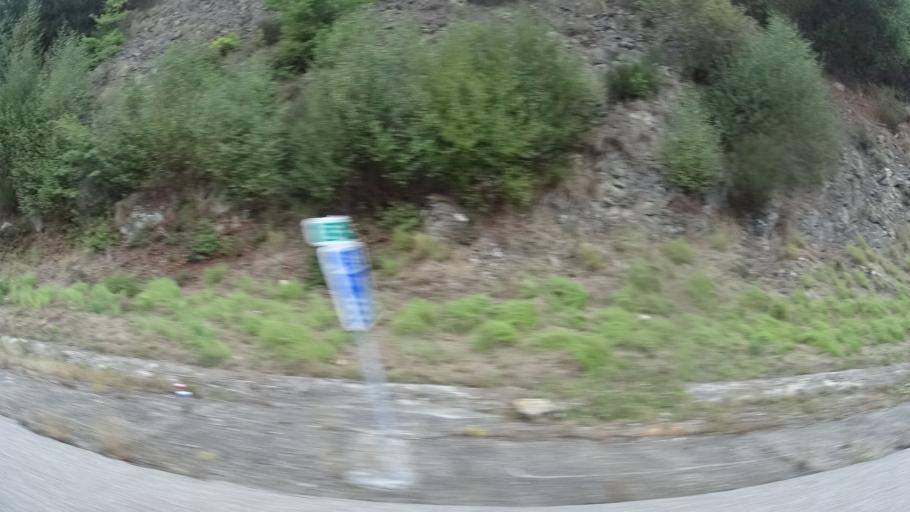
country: ES
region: Galicia
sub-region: Provincia de Lugo
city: Guitiriz
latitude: 43.1803
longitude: -7.8106
